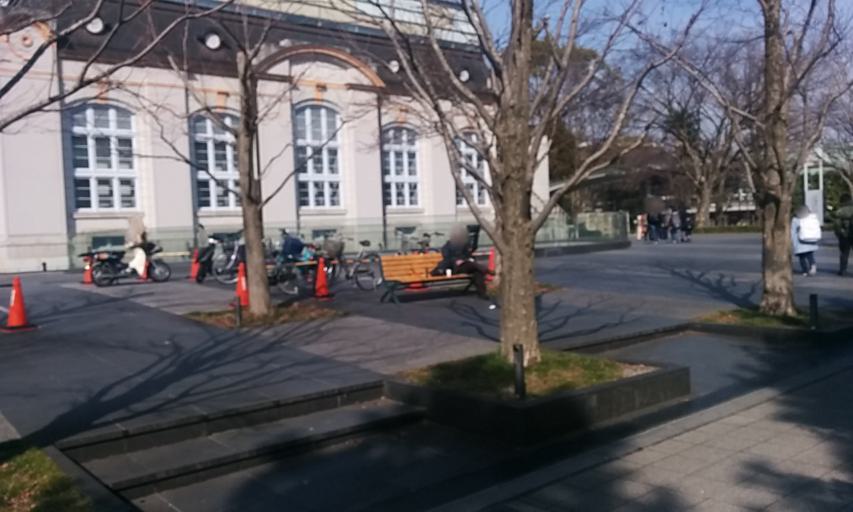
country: JP
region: Kyoto
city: Kyoto
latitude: 35.0128
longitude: 135.7825
